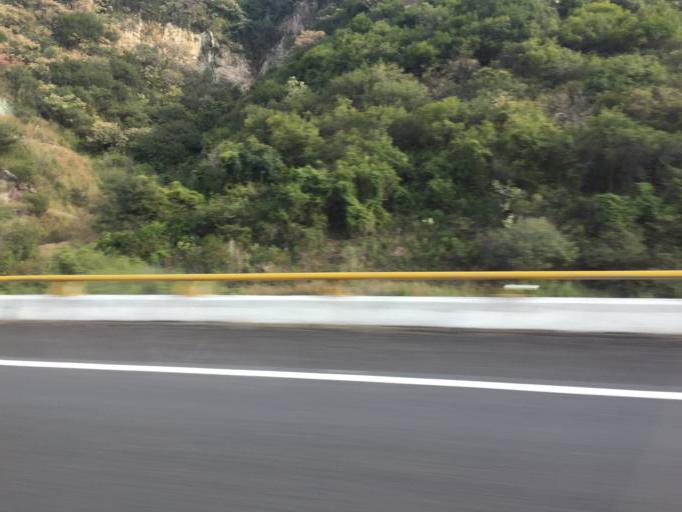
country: MX
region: Michoacan
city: Copandaro de Galeana
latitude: 19.8866
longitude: -101.1857
